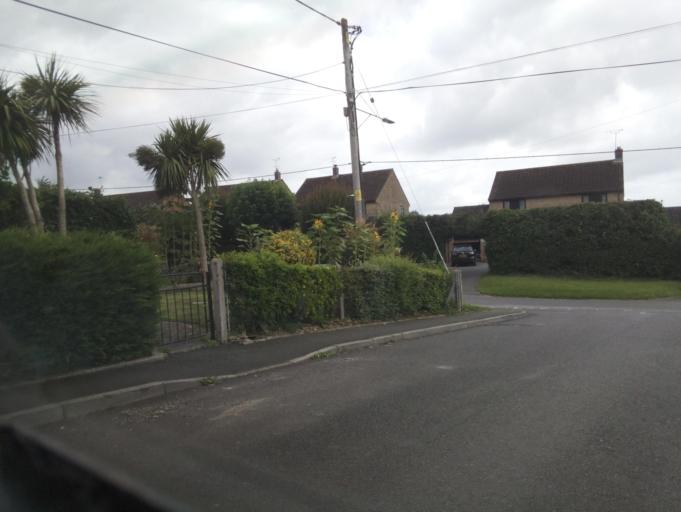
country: GB
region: England
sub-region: Somerset
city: Milborne Port
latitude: 50.9706
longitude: -2.4670
